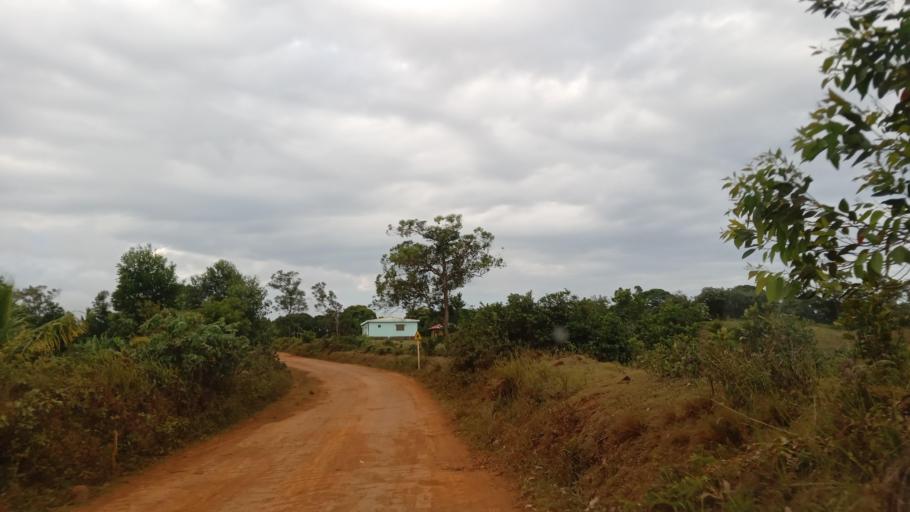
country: MG
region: Atsimo-Atsinanana
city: Vohipaho
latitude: -23.6862
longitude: 47.5752
